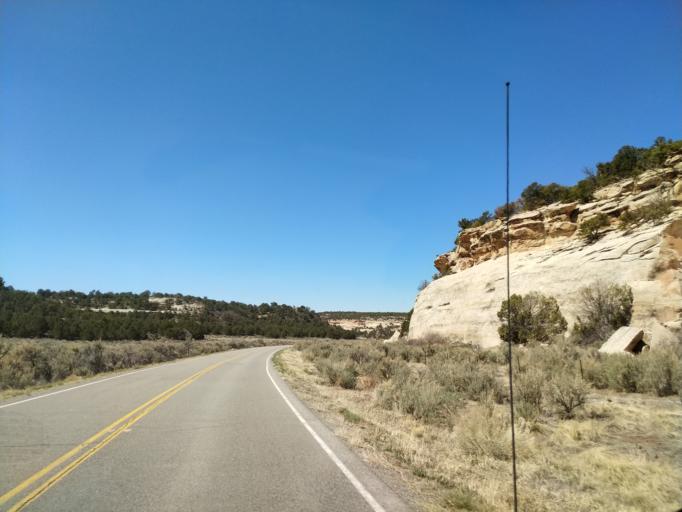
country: US
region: Colorado
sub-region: Mesa County
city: Redlands
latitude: 38.9888
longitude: -108.7782
